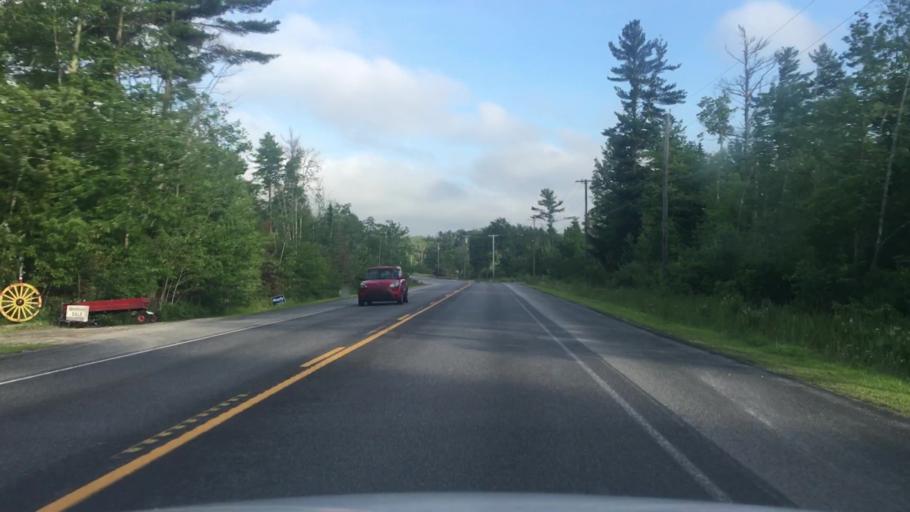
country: US
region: Maine
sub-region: Cumberland County
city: South Windham
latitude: 43.7839
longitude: -70.3914
